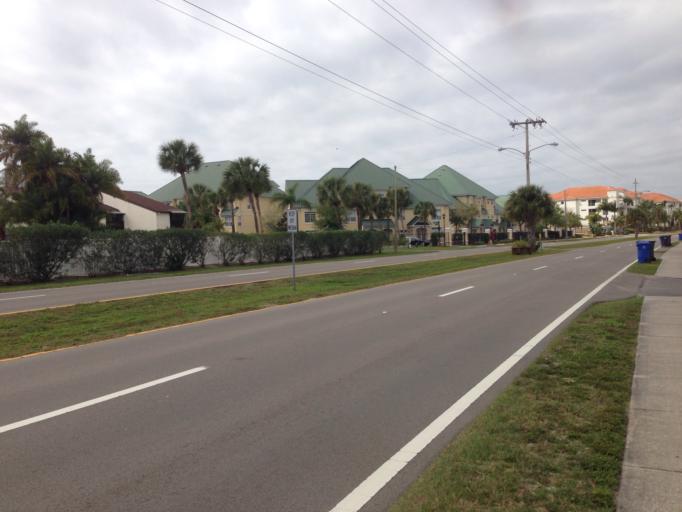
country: US
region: Florida
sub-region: Hillsborough County
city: Apollo Beach
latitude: 27.7775
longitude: -82.4179
